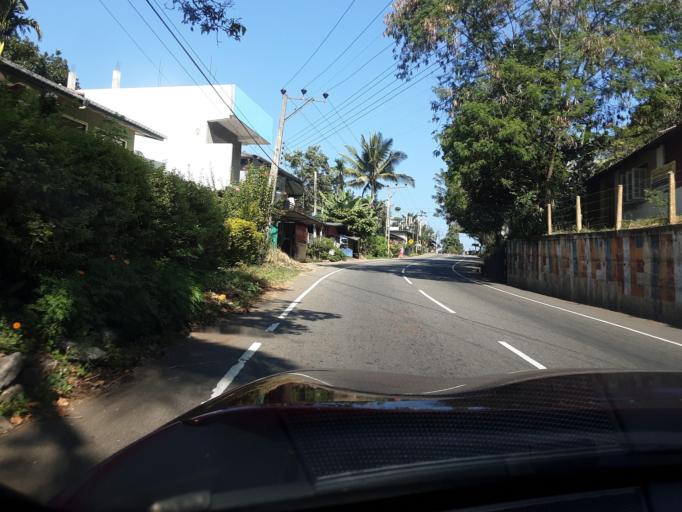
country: LK
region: Uva
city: Badulla
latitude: 7.0116
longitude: 81.0560
